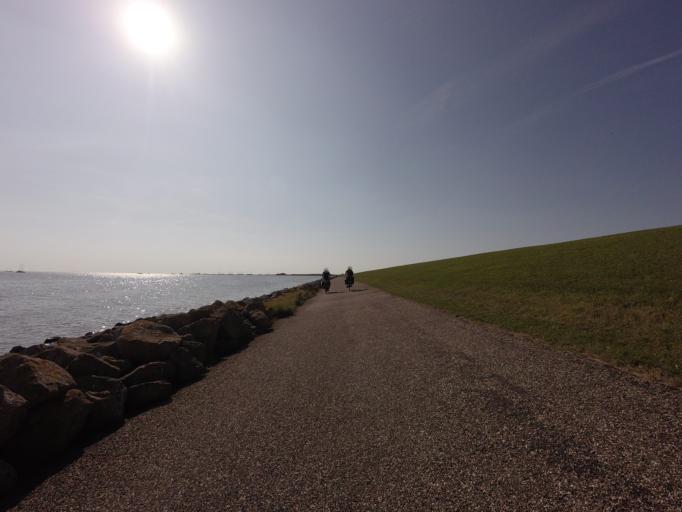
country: NL
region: Friesland
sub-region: Gemeente Schiermonnikoog
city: Schiermonnikoog
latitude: 53.4724
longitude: 6.1815
